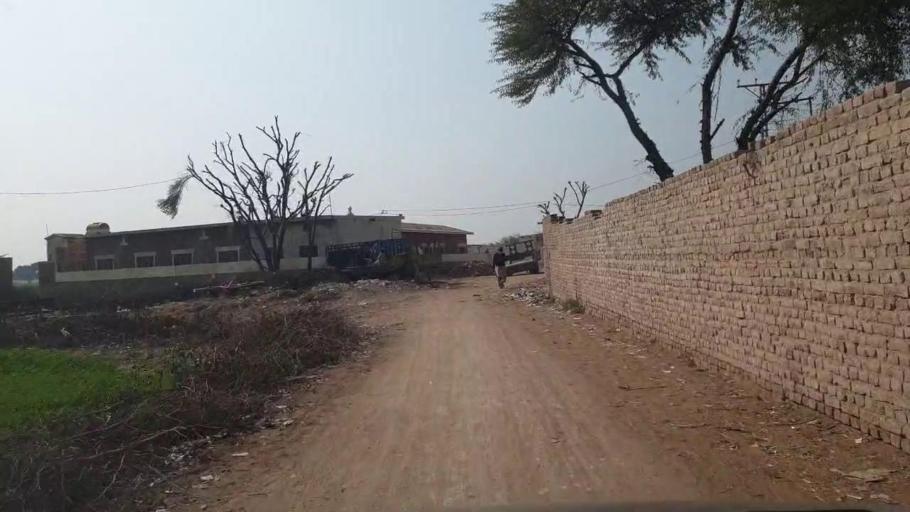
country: PK
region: Sindh
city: Hala
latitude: 25.8332
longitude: 68.4188
